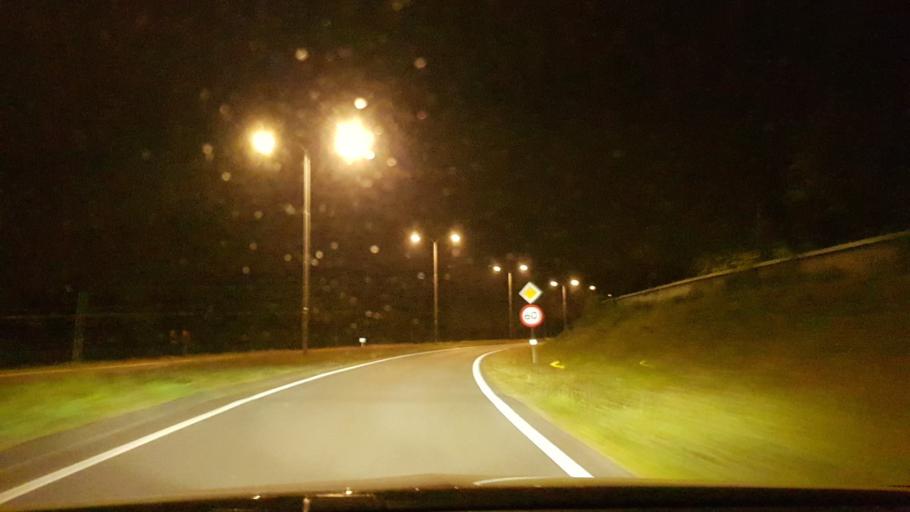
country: NL
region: South Holland
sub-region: Gemeente Lisse
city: Lisse
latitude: 52.2567
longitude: 4.5463
